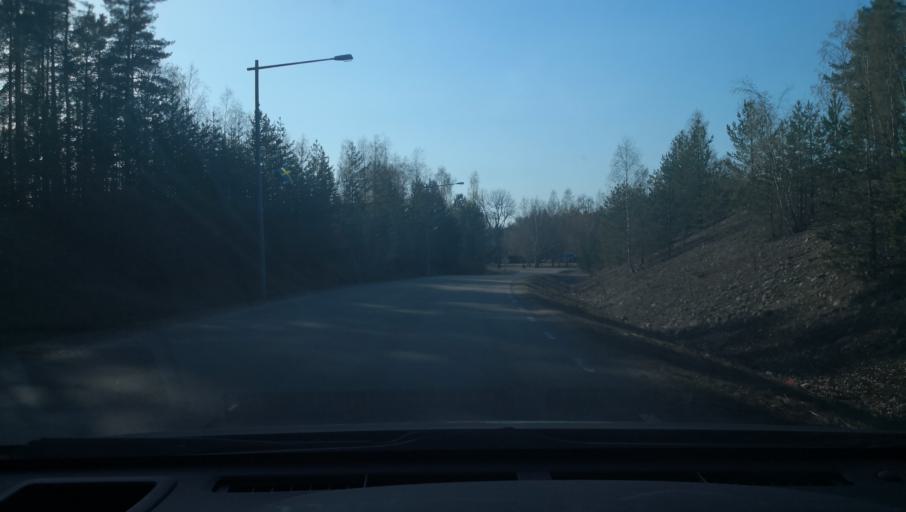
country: SE
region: Uppsala
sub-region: Heby Kommun
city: Tarnsjo
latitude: 60.1547
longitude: 16.9335
